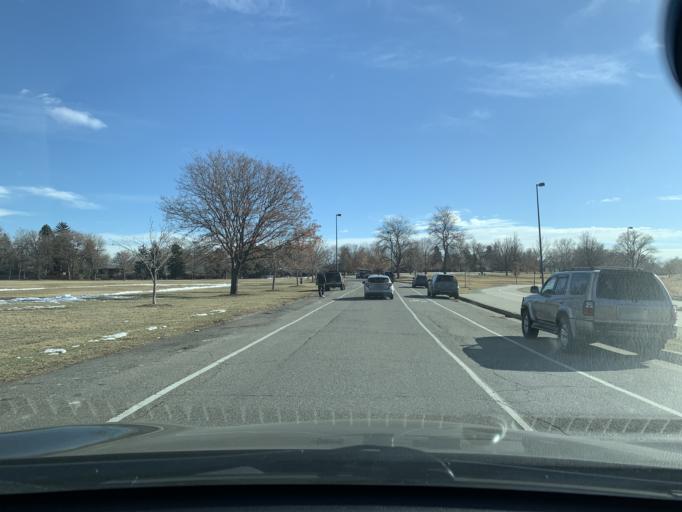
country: US
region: Colorado
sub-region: Jefferson County
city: Edgewater
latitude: 39.7529
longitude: -105.0457
